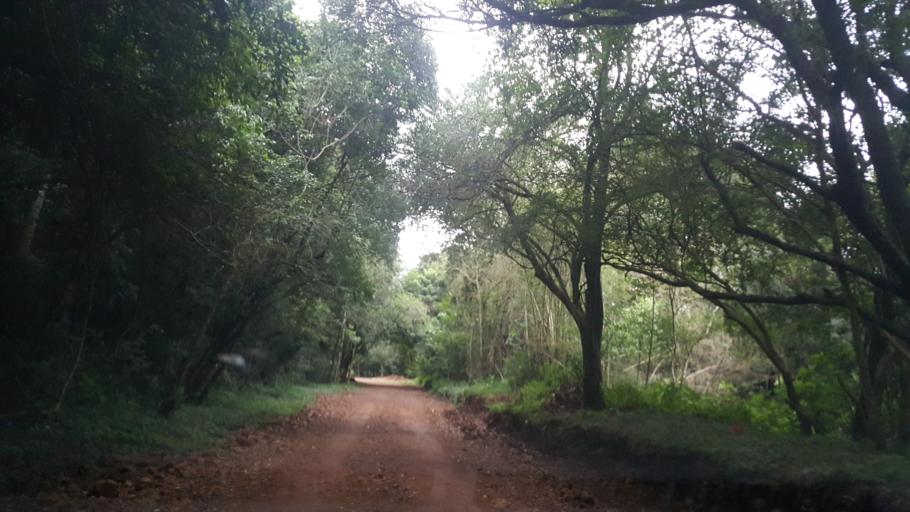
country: AR
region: Misiones
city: Capiovi
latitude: -26.9254
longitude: -55.0566
